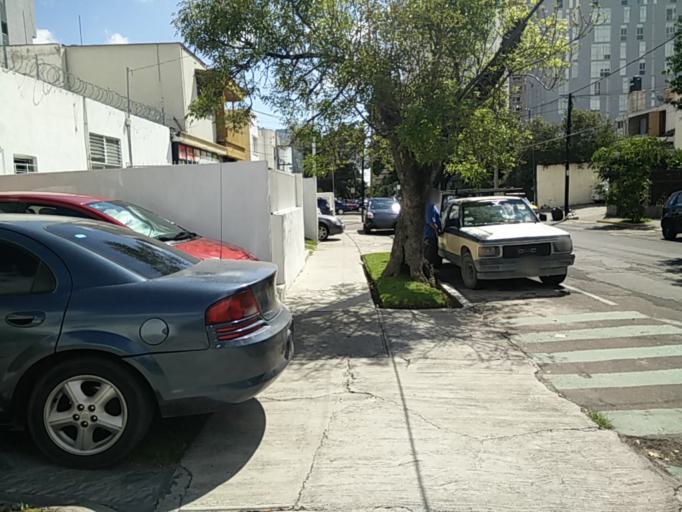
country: MX
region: Jalisco
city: Guadalajara
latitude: 20.6684
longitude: -103.3713
